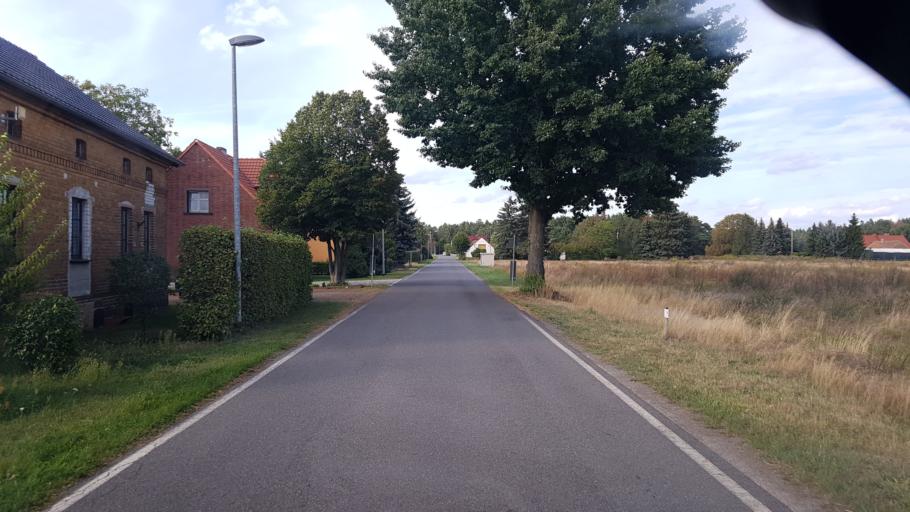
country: DE
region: Brandenburg
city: Neupetershain
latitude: 51.5834
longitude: 14.1132
